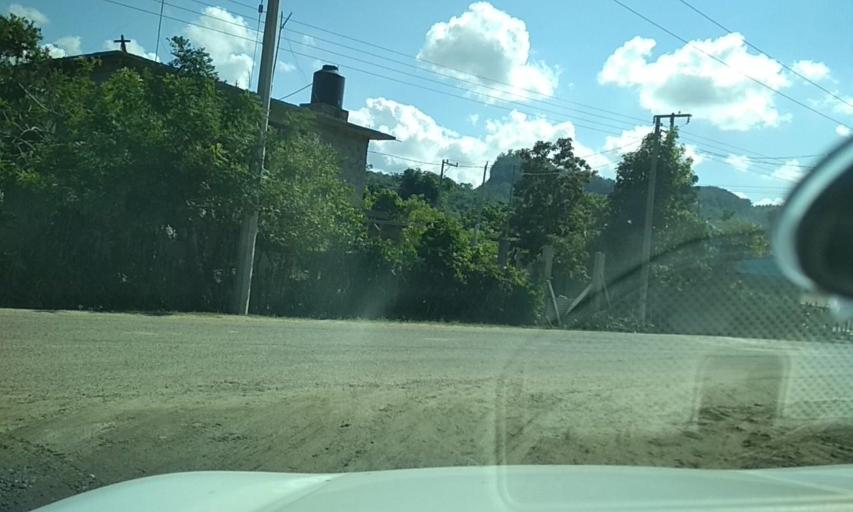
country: MX
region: Veracruz
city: Cazones de Herrera
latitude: 20.6415
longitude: -97.3086
